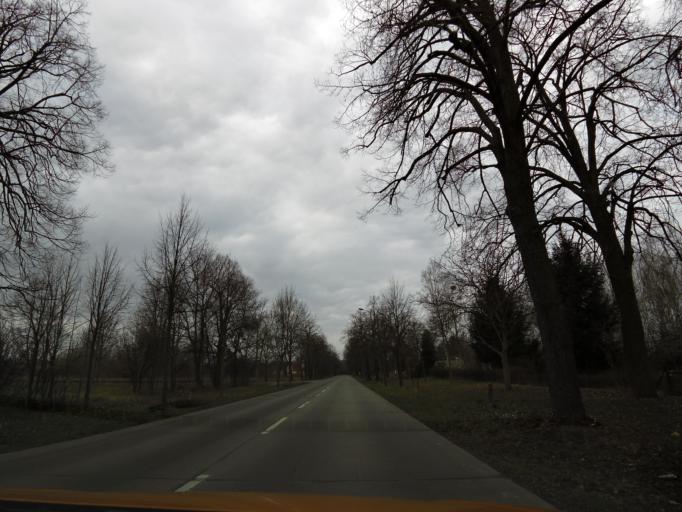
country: DE
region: Brandenburg
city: Potsdam
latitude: 52.4244
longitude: 13.0287
